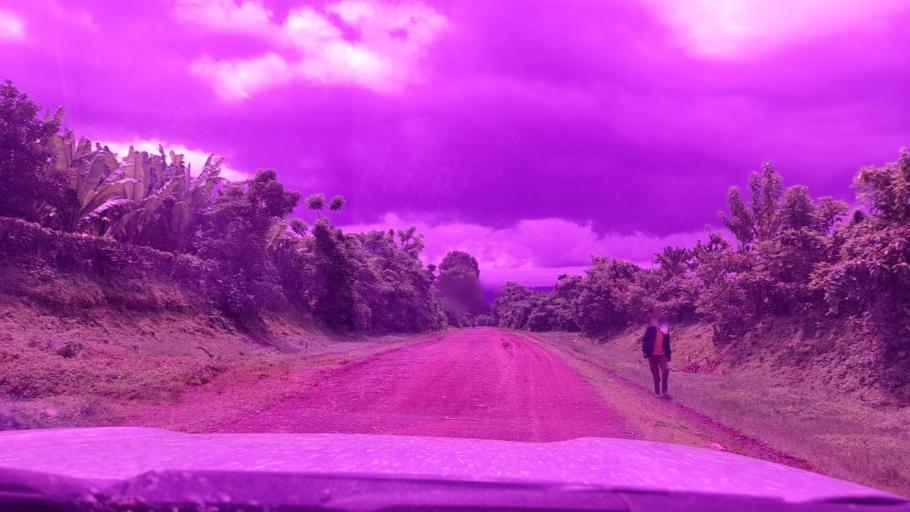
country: ET
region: Southern Nations, Nationalities, and People's Region
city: Tippi
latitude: 7.6243
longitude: 35.5820
